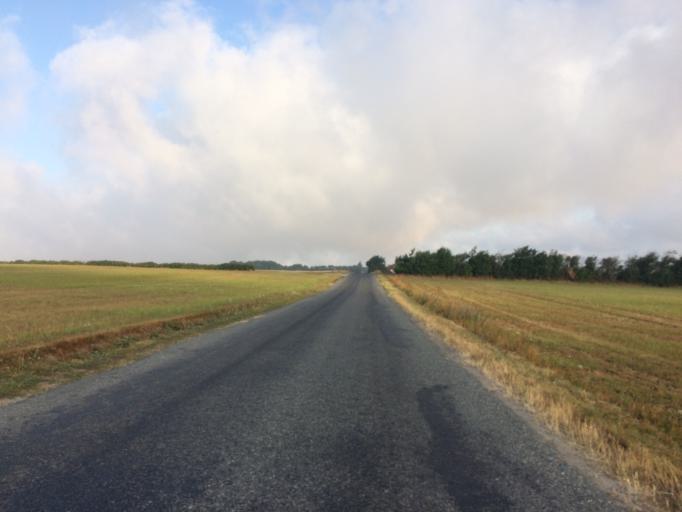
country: DK
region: Central Jutland
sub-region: Holstebro Kommune
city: Vinderup
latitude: 56.5913
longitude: 8.7519
